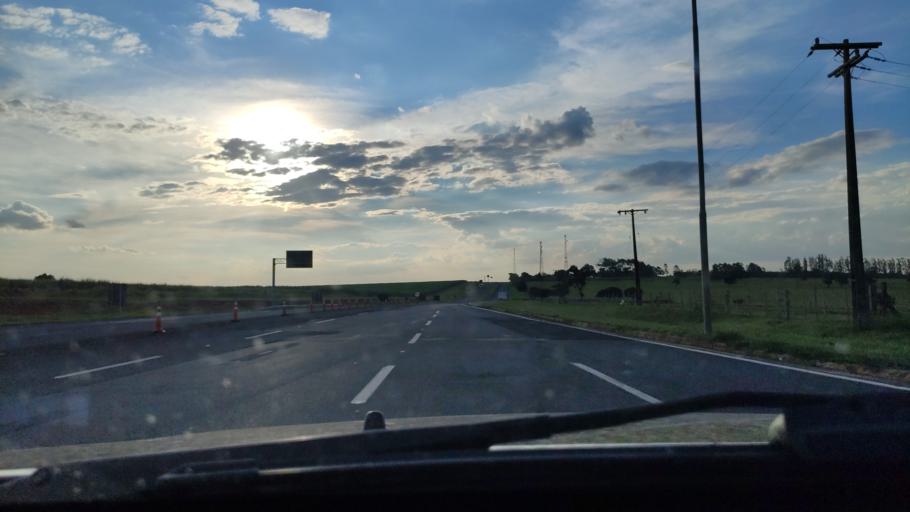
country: BR
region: Sao Paulo
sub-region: Rancharia
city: Rancharia
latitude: -22.4344
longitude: -51.0096
